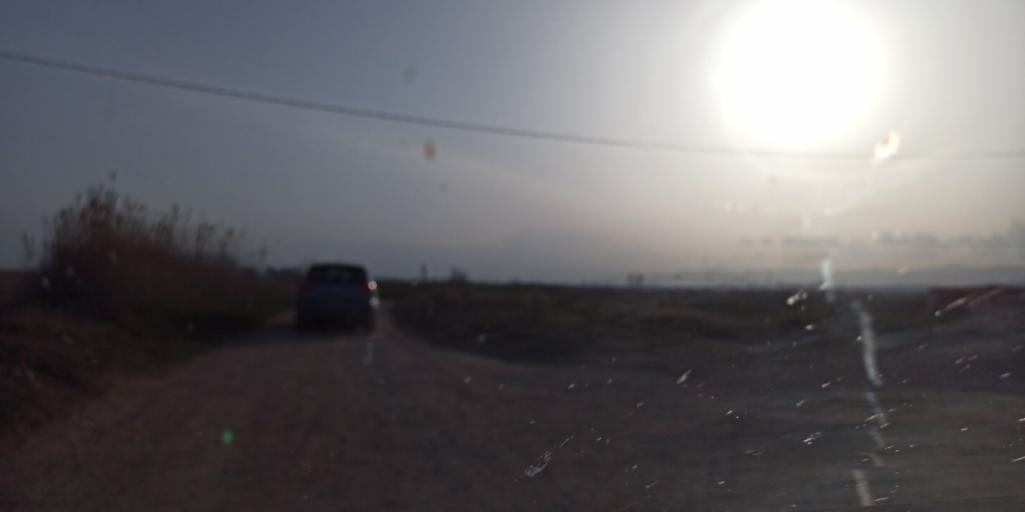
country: ES
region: Catalonia
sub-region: Provincia de Tarragona
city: L'Ampolla
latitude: 40.7856
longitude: 0.7091
